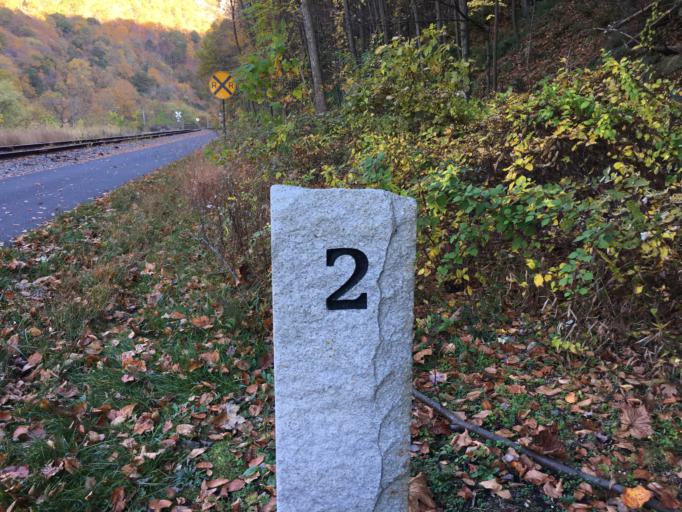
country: US
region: Maryland
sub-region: Allegany County
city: La Vale
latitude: 39.6689
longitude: -78.7872
